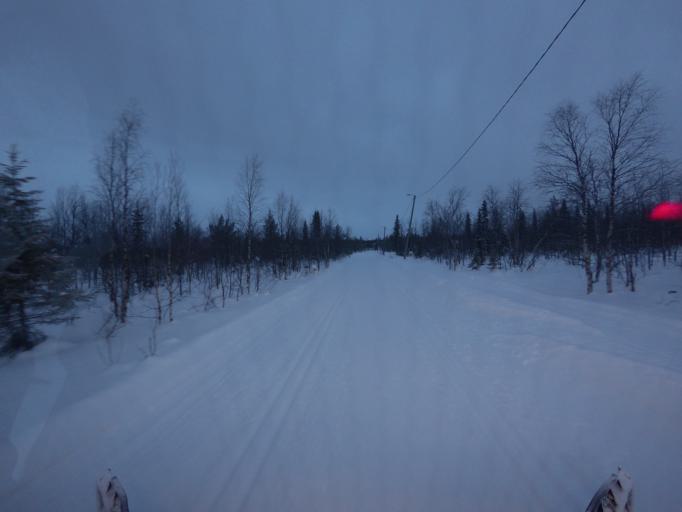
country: FI
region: Lapland
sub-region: Tunturi-Lappi
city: Kolari
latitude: 67.6143
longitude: 24.1660
